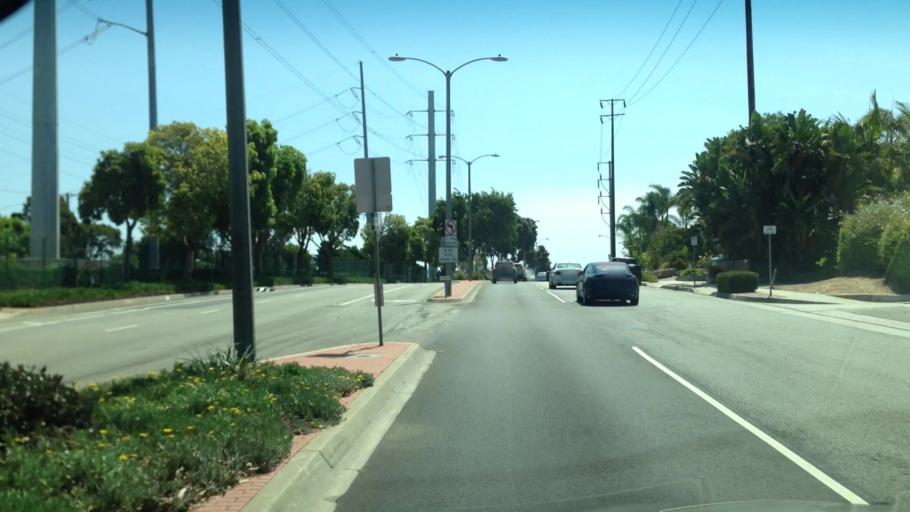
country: US
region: California
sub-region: Los Angeles County
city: Manhattan Beach
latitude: 33.9020
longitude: -118.3993
